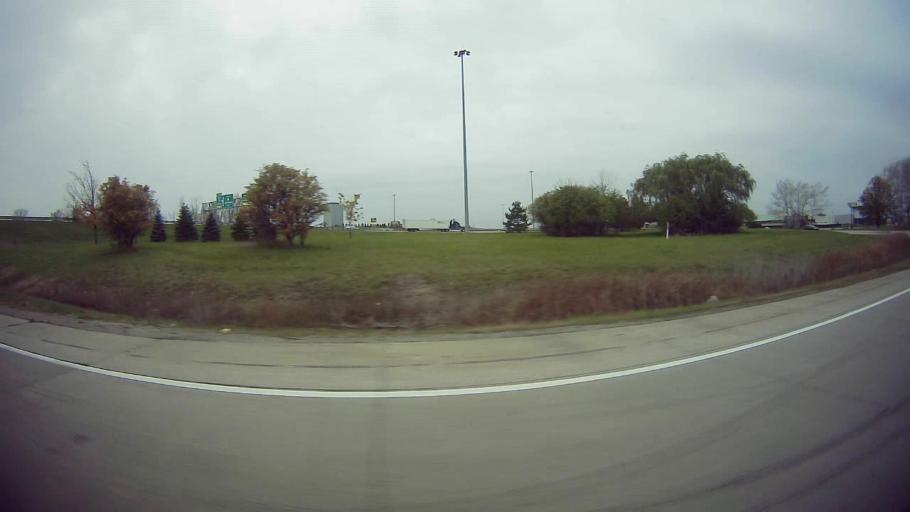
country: US
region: Michigan
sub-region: Oakland County
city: Bingham Farms
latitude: 42.4926
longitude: -83.2850
